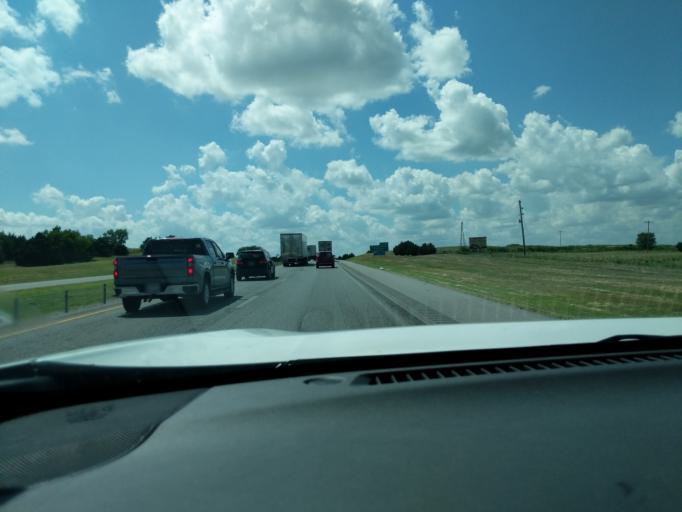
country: US
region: Oklahoma
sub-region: Caddo County
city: Hinton
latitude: 35.5270
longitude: -98.3223
